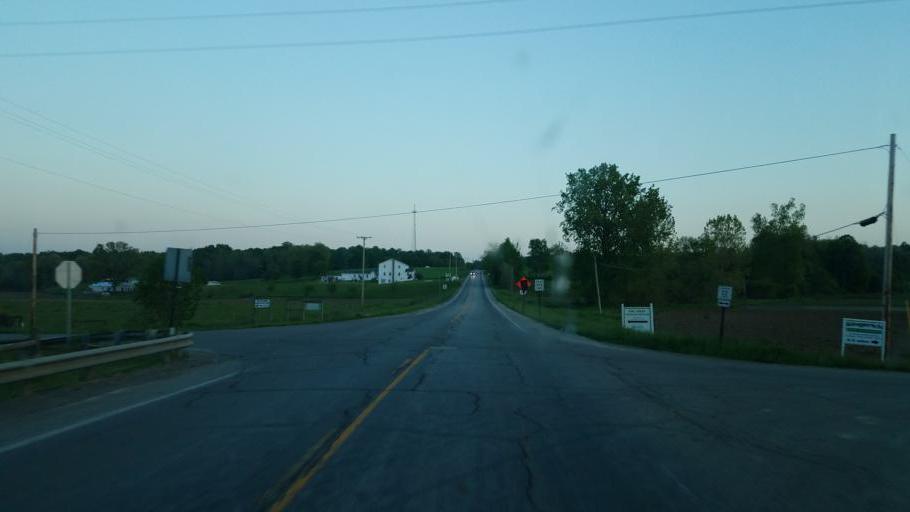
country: US
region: Ohio
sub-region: Knox County
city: Fredericktown
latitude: 40.5504
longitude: -82.6620
